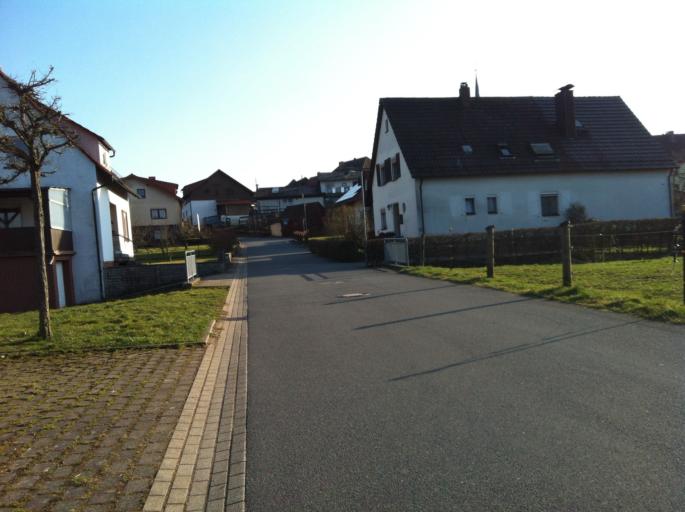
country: DE
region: Baden-Wuerttemberg
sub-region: Karlsruhe Region
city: Mudau
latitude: 49.5350
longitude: 9.2070
